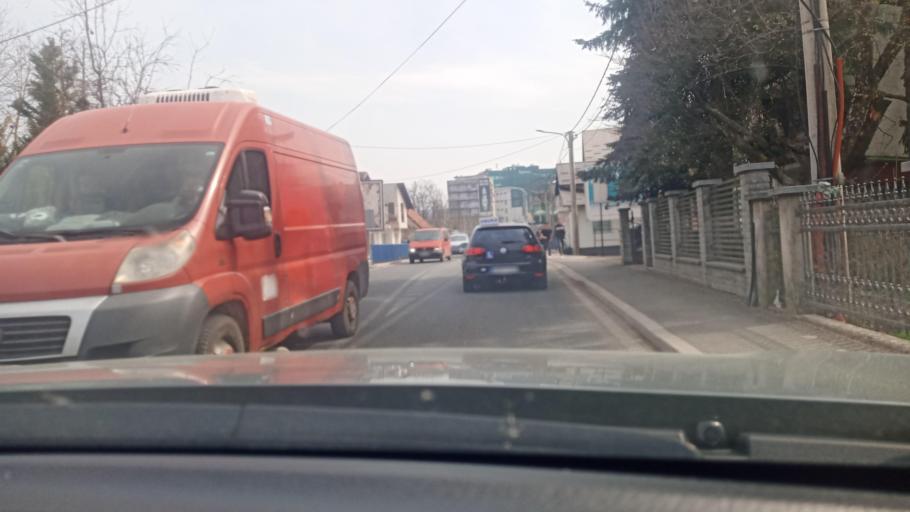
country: BA
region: Federation of Bosnia and Herzegovina
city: Bihac
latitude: 44.8178
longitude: 15.8662
